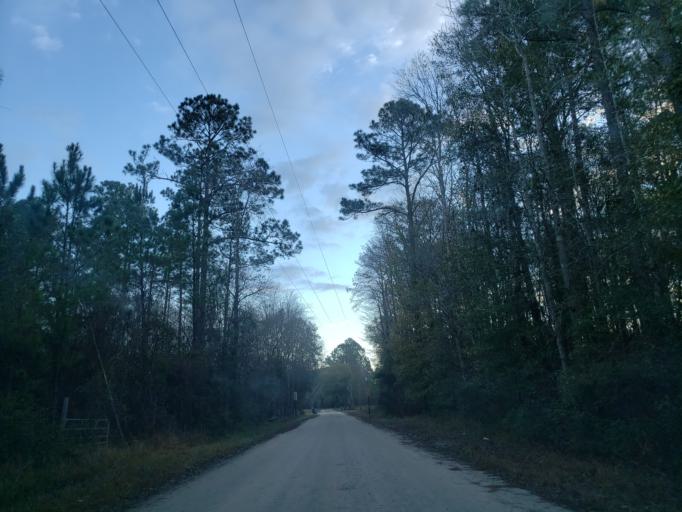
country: US
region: Georgia
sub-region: Chatham County
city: Bloomingdale
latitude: 32.1176
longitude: -81.3412
